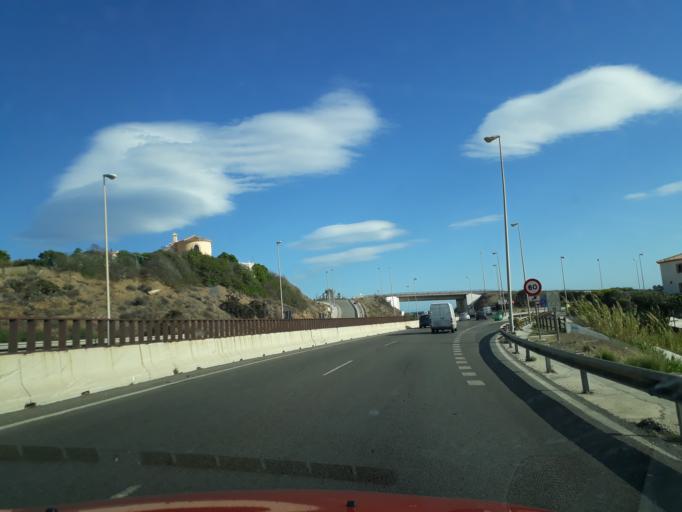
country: ES
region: Andalusia
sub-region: Provincia de Malaga
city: Fuengirola
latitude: 36.5079
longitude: -4.6457
